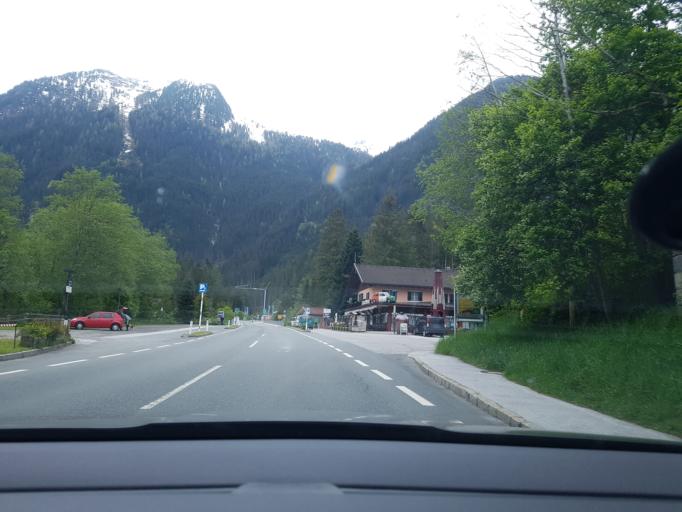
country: AT
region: Salzburg
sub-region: Politischer Bezirk Zell am See
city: Krimml
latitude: 47.2158
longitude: 12.1719
